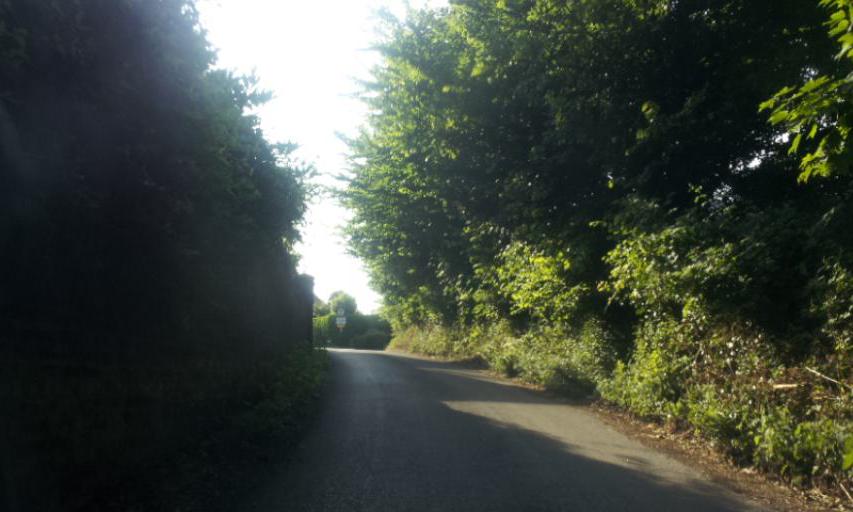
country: GB
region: England
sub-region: Kent
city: Boxley
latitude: 51.2911
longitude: 0.5904
